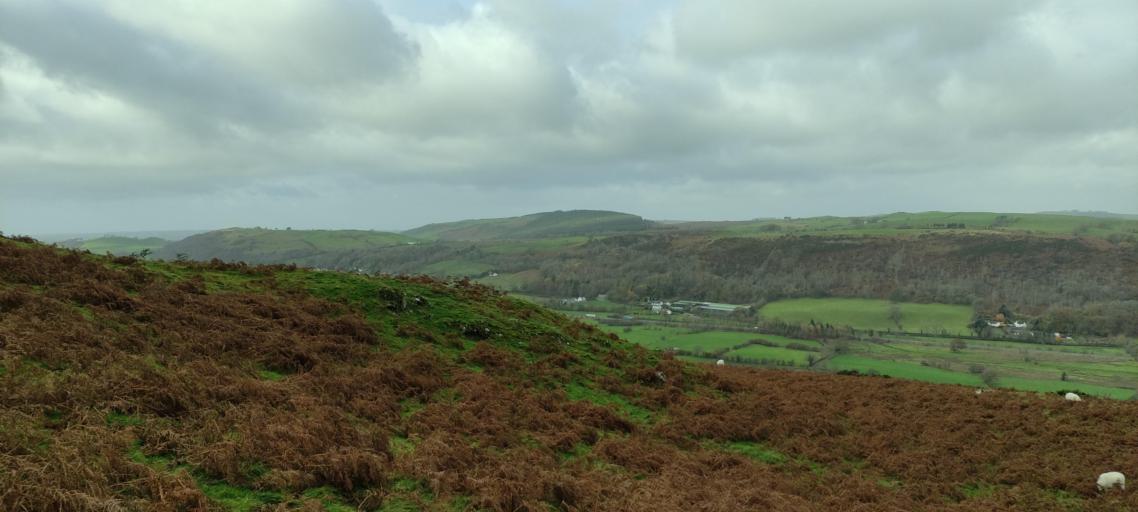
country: GB
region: England
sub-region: Cumbria
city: Cockermouth
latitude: 54.6560
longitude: -3.2612
